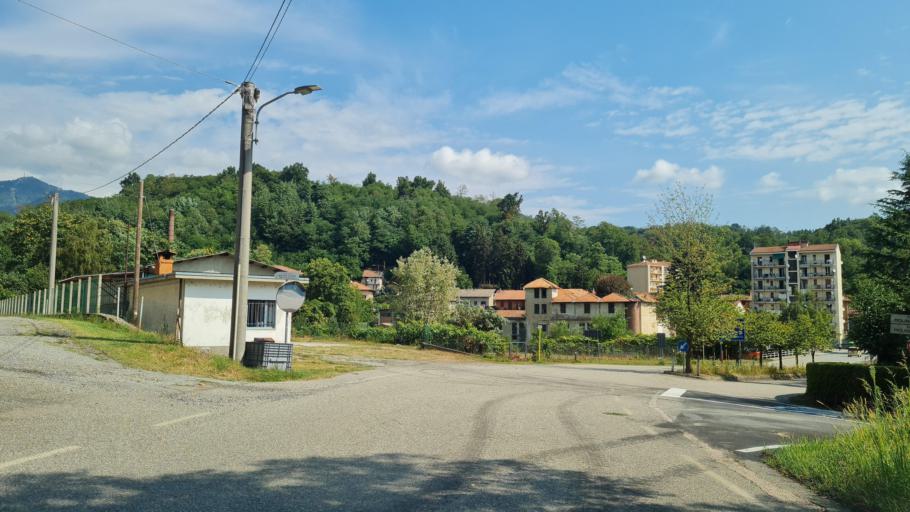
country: IT
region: Piedmont
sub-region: Provincia di Biella
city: Fontanella-Ozino
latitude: 45.6187
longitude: 8.1566
